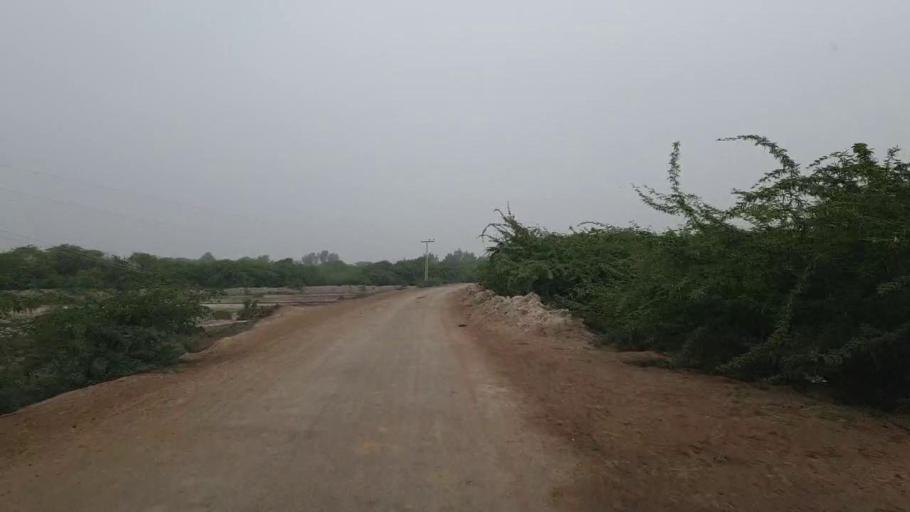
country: PK
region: Sindh
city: Badin
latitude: 24.5848
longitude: 68.6666
